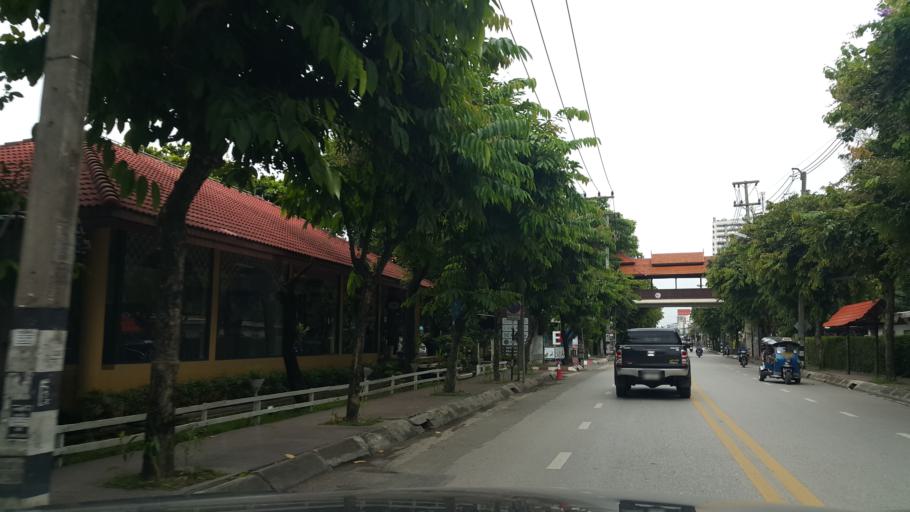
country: TH
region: Chiang Mai
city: Chiang Mai
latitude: 18.7955
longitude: 99.0047
